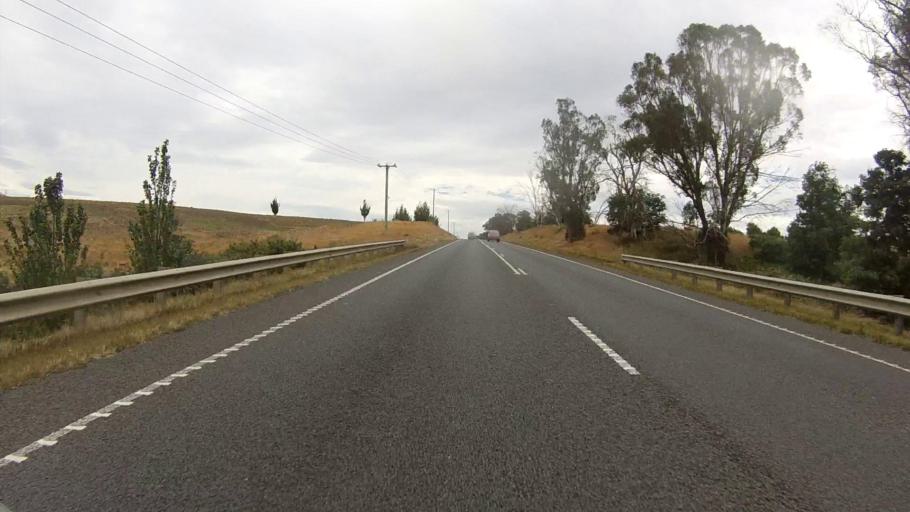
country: AU
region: Tasmania
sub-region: Northern Midlands
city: Evandale
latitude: -41.7004
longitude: 147.2916
